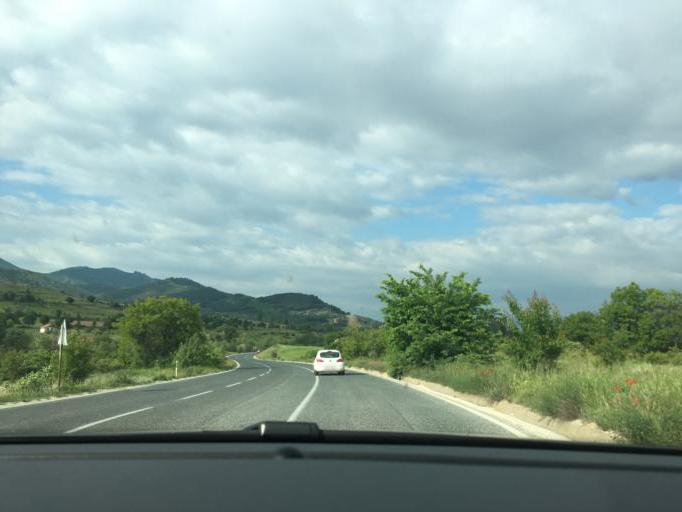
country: MK
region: Prilep
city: Prilep
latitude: 41.3674
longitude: 21.6100
